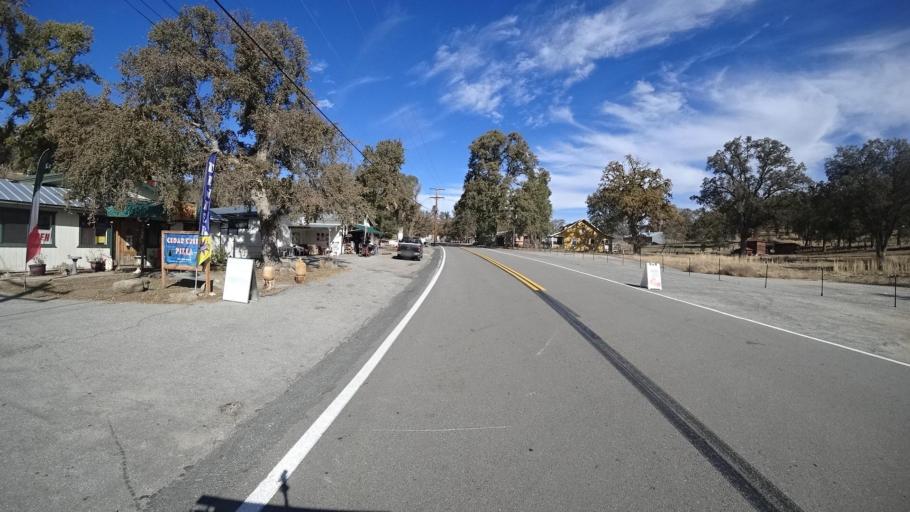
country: US
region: California
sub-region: Kern County
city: Alta Sierra
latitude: 35.7163
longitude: -118.7274
